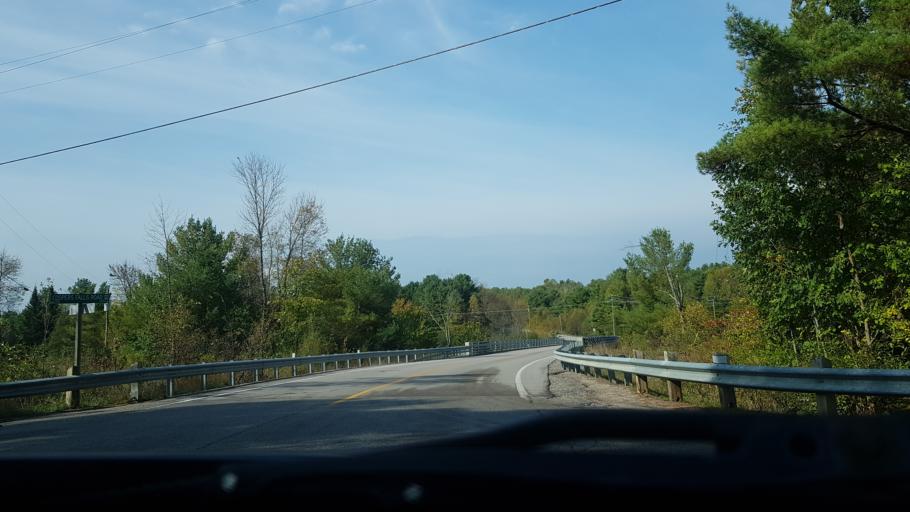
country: CA
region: Ontario
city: Gravenhurst
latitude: 44.7751
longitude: -79.2955
